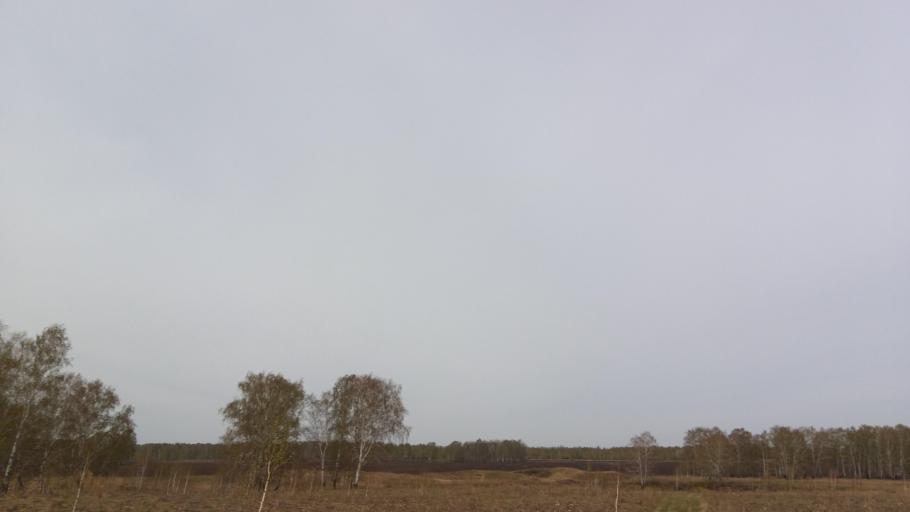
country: RU
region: Chelyabinsk
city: Timiryazevskiy
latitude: 55.0111
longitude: 60.8636
